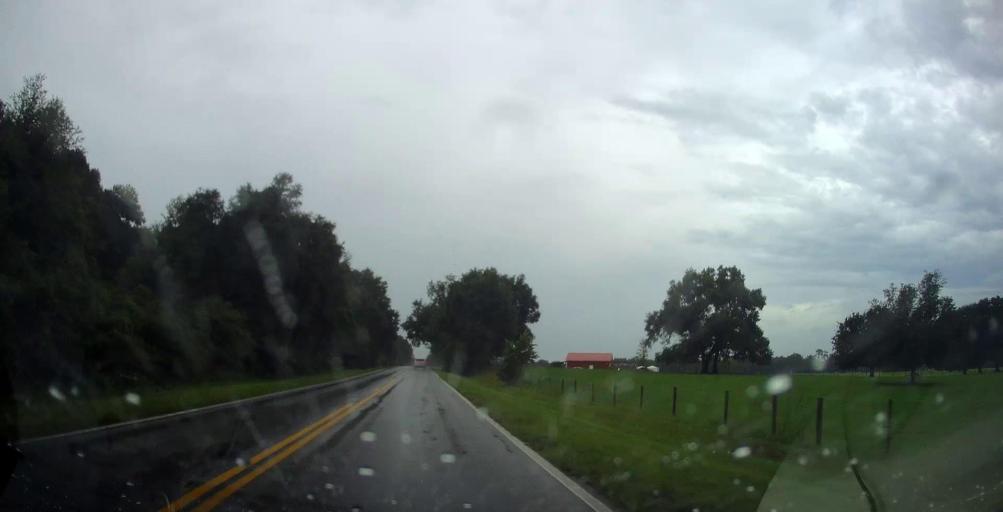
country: US
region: Florida
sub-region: Marion County
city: Ocala
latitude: 29.2577
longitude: -82.0932
